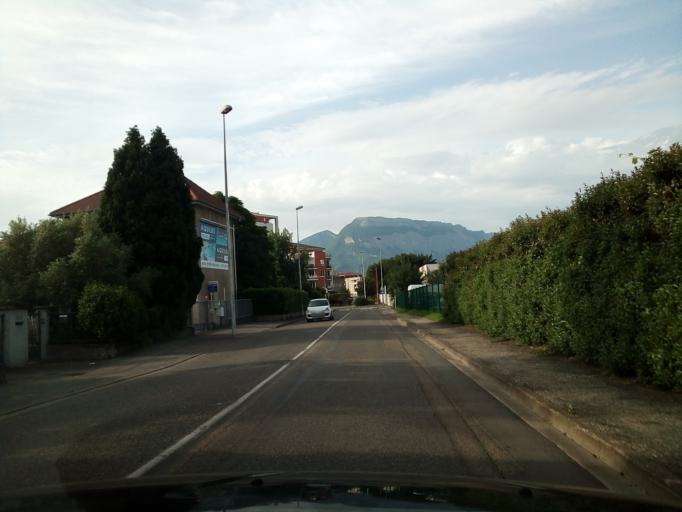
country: FR
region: Rhone-Alpes
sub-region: Departement de l'Isere
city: Eybens
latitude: 45.1626
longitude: 5.7419
